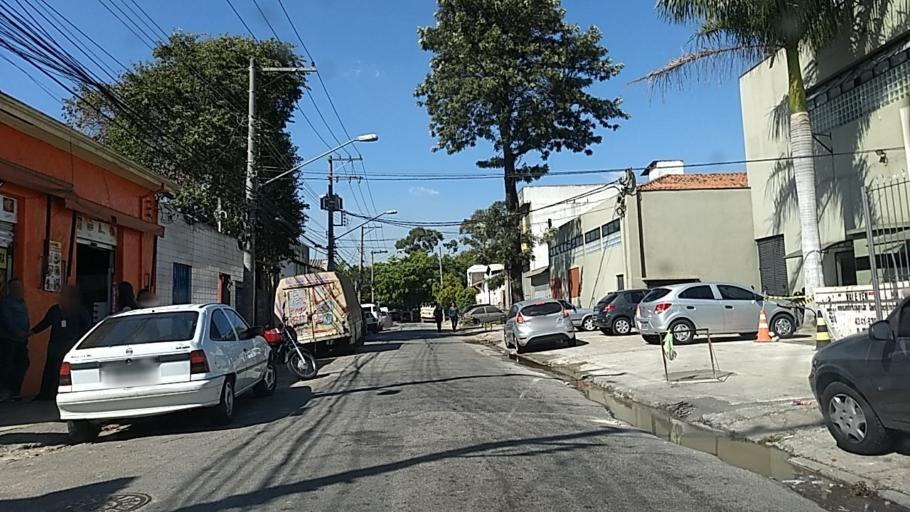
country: BR
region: Sao Paulo
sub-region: Sao Paulo
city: Sao Paulo
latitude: -23.5207
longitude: -46.6092
